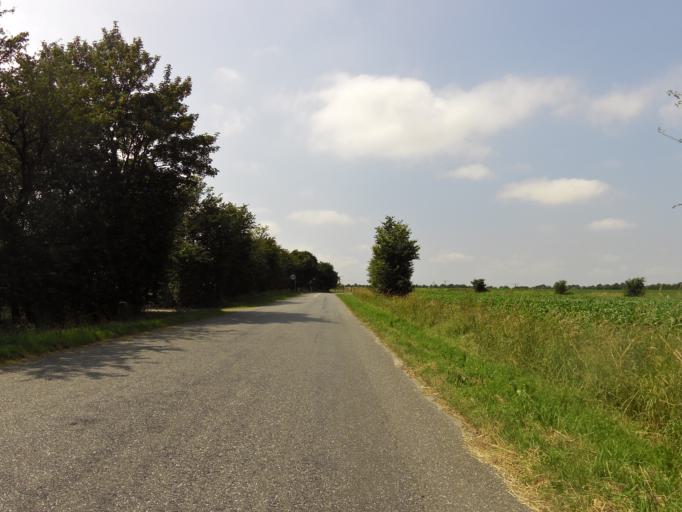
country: DK
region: South Denmark
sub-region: Tonder Kommune
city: Toftlund
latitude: 55.1435
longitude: 9.1968
